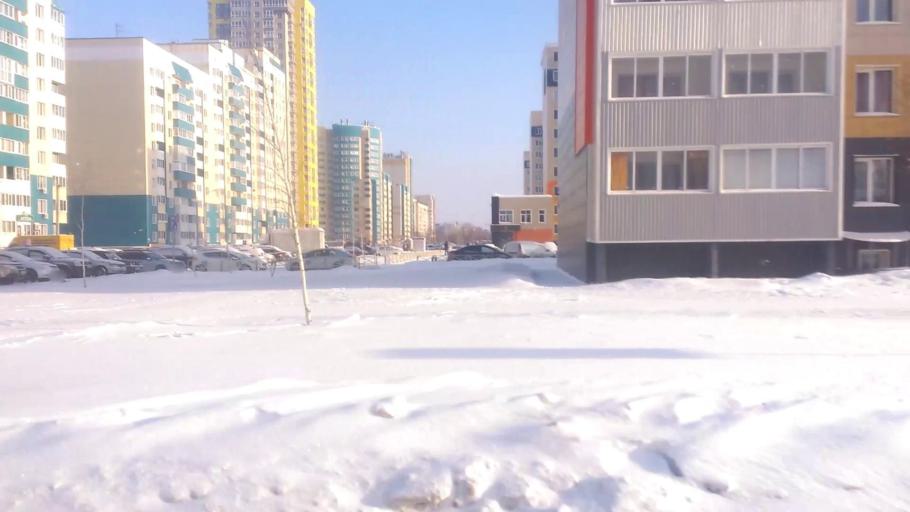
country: RU
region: Altai Krai
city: Novosilikatnyy
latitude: 53.3405
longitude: 83.6546
